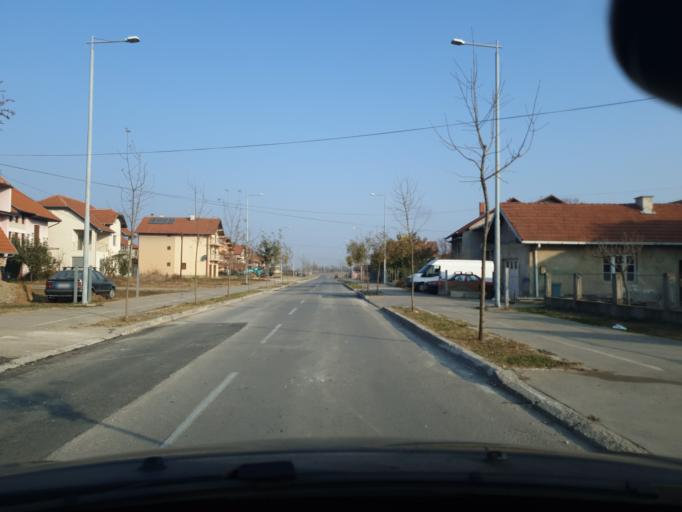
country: RS
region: Central Serbia
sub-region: Jablanicki Okrug
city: Leskovac
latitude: 42.9995
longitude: 21.9237
